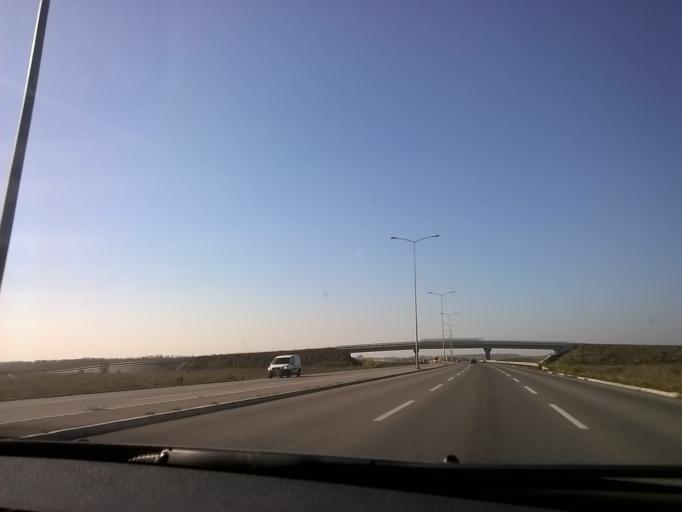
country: RS
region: Central Serbia
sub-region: Belgrade
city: Zemun
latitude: 44.8967
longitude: 20.4184
